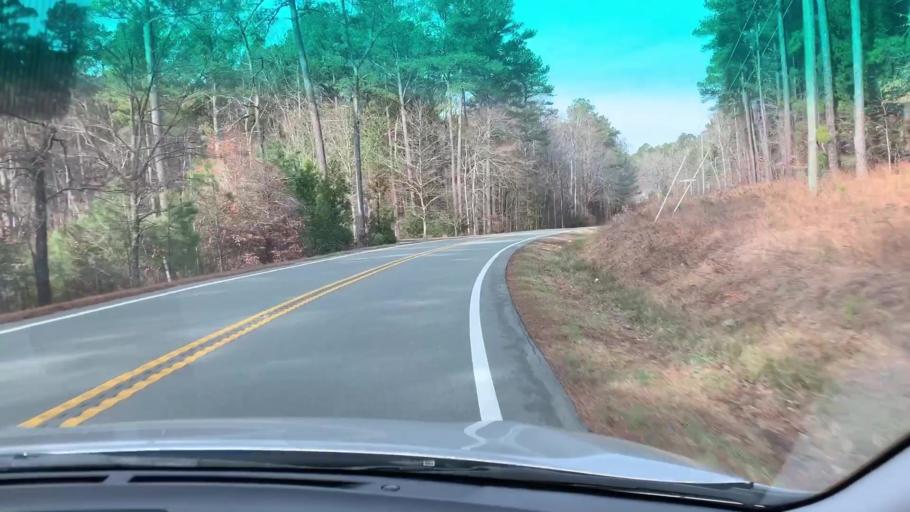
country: US
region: North Carolina
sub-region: Wake County
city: Green Level
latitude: 35.8473
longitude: -78.9305
